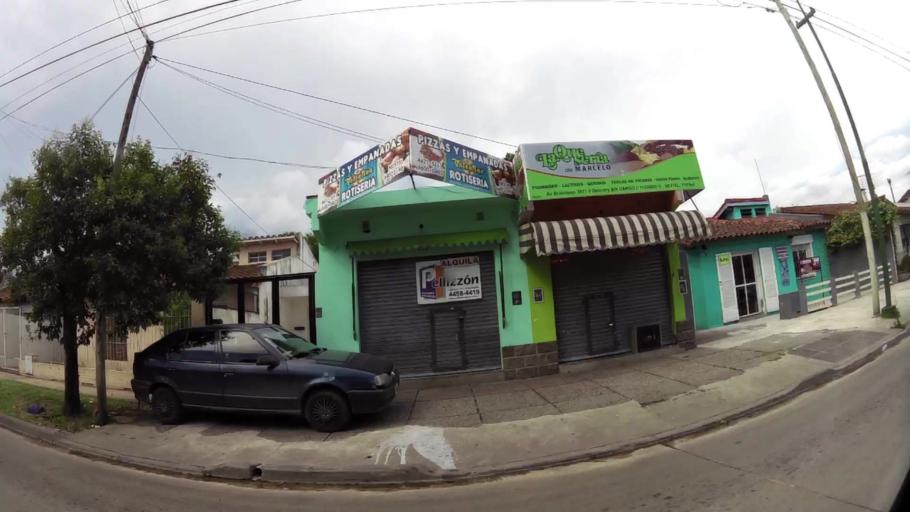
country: AR
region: Buenos Aires
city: Ituzaingo
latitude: -34.6372
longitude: -58.6929
